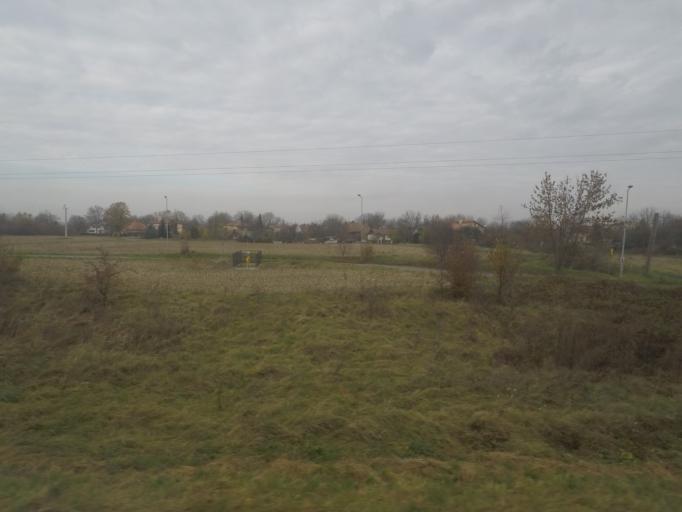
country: PL
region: Subcarpathian Voivodeship
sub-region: Powiat przemyski
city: Zurawica
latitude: 49.7845
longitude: 22.8133
